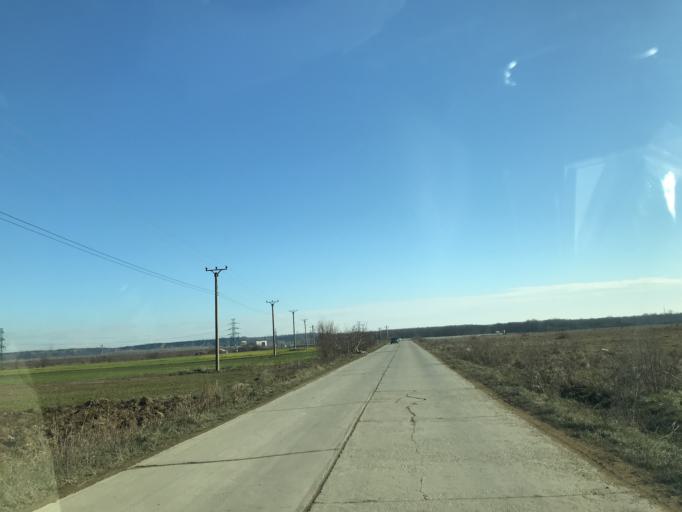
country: RO
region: Olt
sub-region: Comuna Slatioara
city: Slatioara
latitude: 44.3933
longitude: 24.3331
